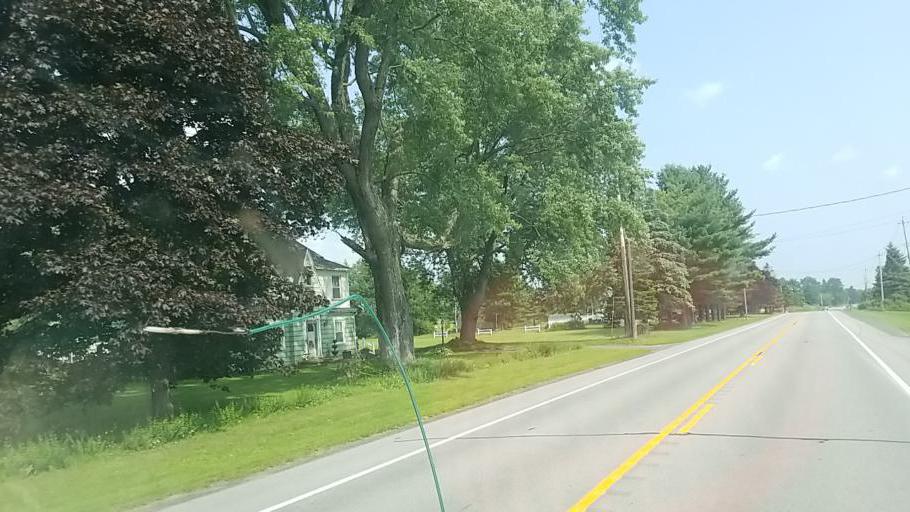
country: US
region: New York
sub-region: Fulton County
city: Johnstown
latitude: 42.9958
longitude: -74.3423
